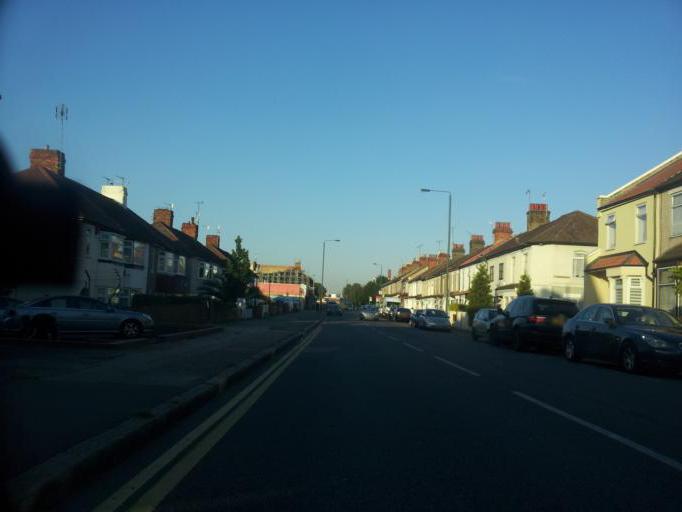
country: GB
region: England
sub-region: Greater London
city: Belvedere
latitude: 51.4913
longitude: 0.1459
